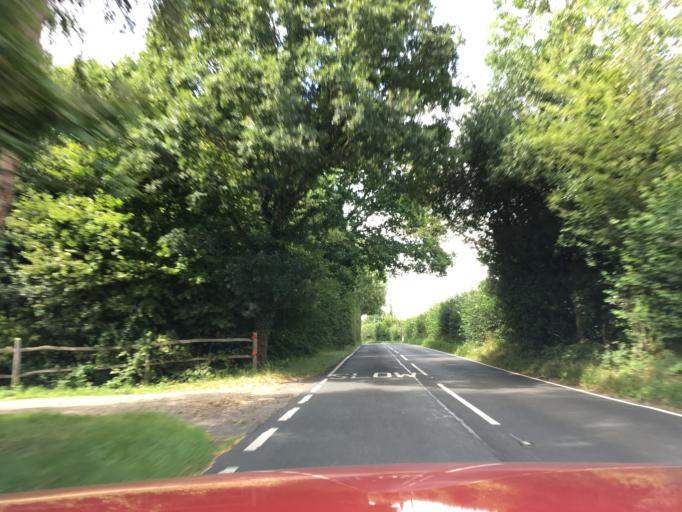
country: GB
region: England
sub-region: Kent
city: Edenbridge
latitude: 51.1268
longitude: 0.1142
